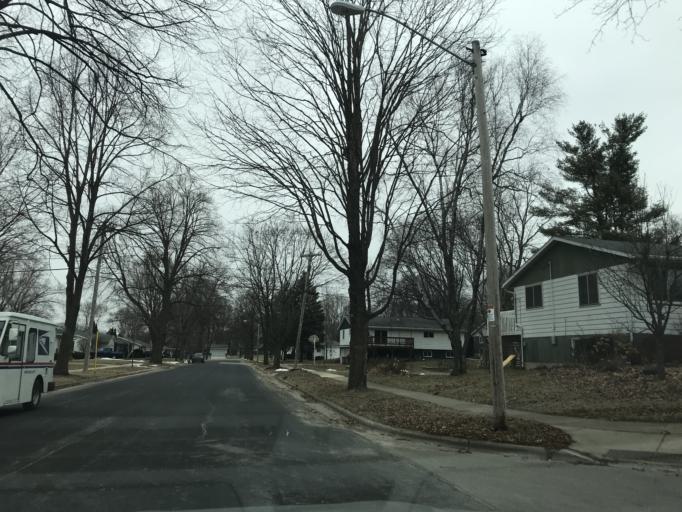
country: US
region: Wisconsin
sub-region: Dane County
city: Monona
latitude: 43.0928
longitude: -89.3010
